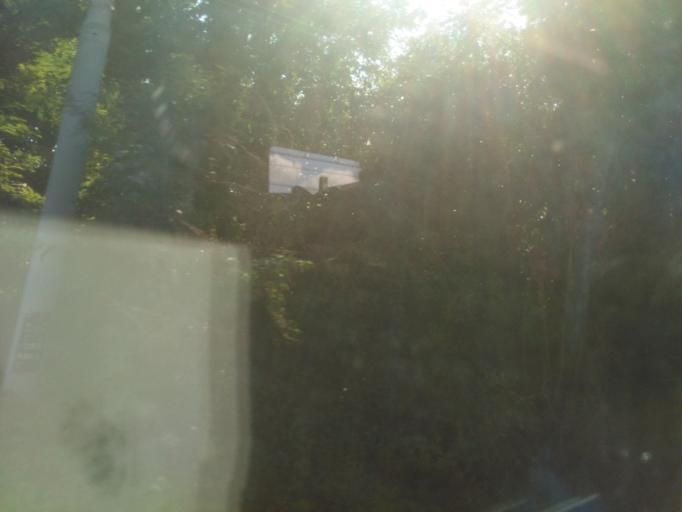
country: IT
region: Lombardy
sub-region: Citta metropolitana di Milano
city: San Bovio-San Felice
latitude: 45.4839
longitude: 9.3181
